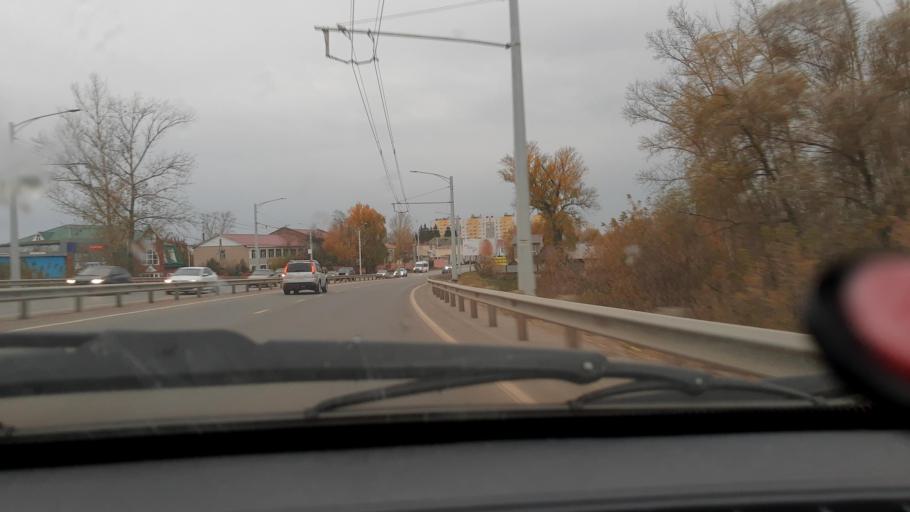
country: RU
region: Bashkortostan
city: Mikhaylovka
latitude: 54.7758
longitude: 55.8929
